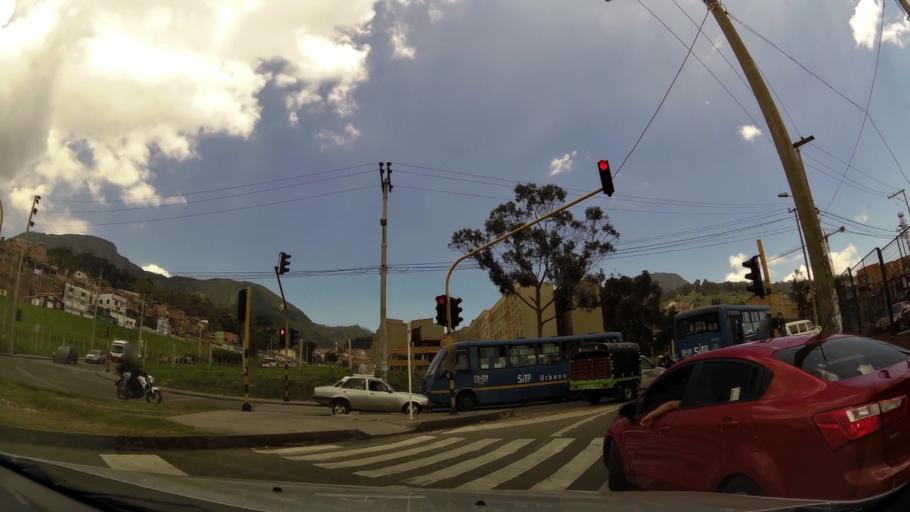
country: CO
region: Bogota D.C.
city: Bogota
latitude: 4.5728
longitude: -74.0793
